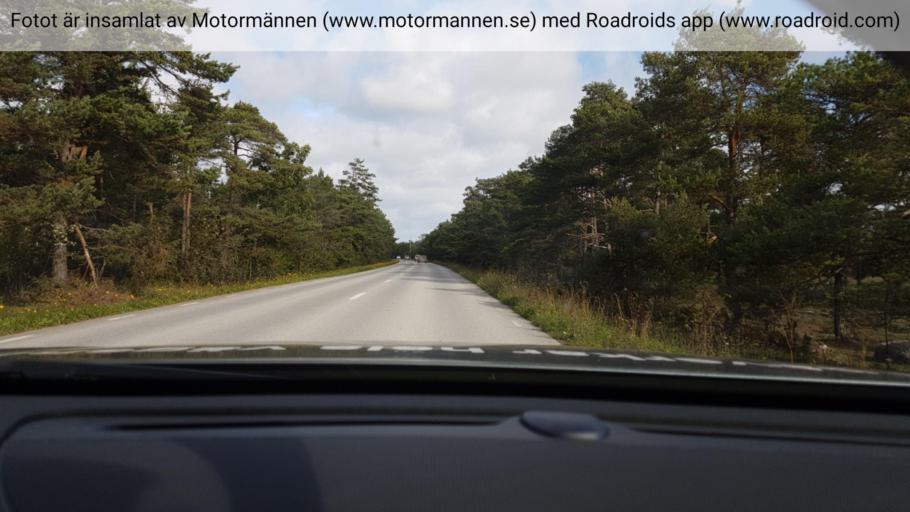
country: SE
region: Gotland
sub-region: Gotland
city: Slite
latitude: 57.8815
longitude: 19.0878
